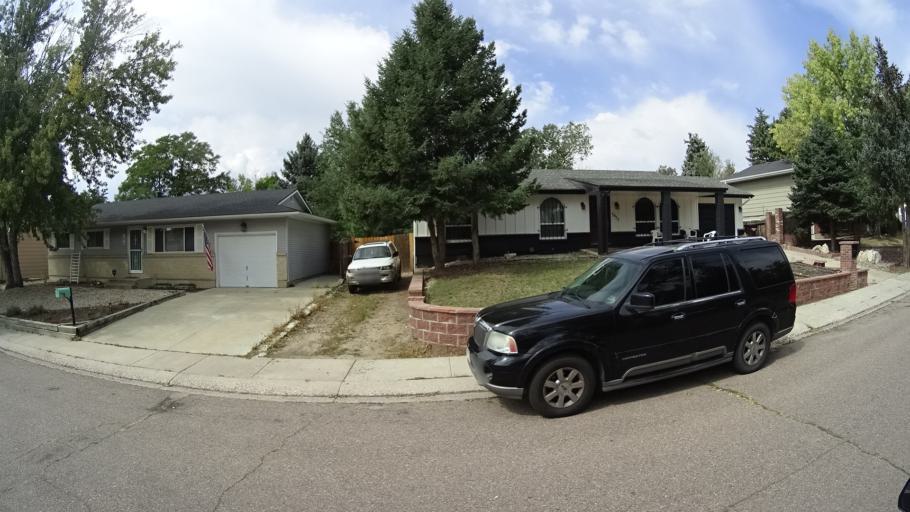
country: US
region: Colorado
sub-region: El Paso County
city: Cimarron Hills
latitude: 38.8483
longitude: -104.7405
